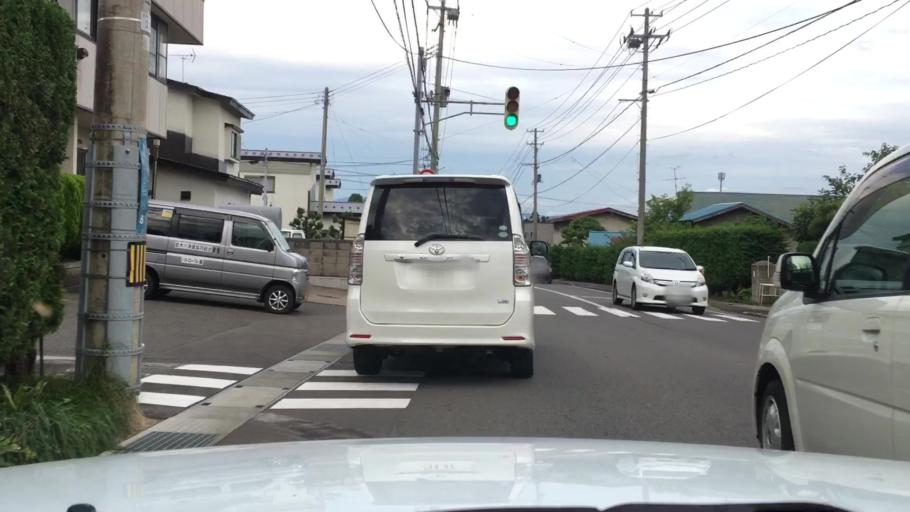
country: JP
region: Aomori
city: Hirosaki
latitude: 40.5867
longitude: 140.4621
